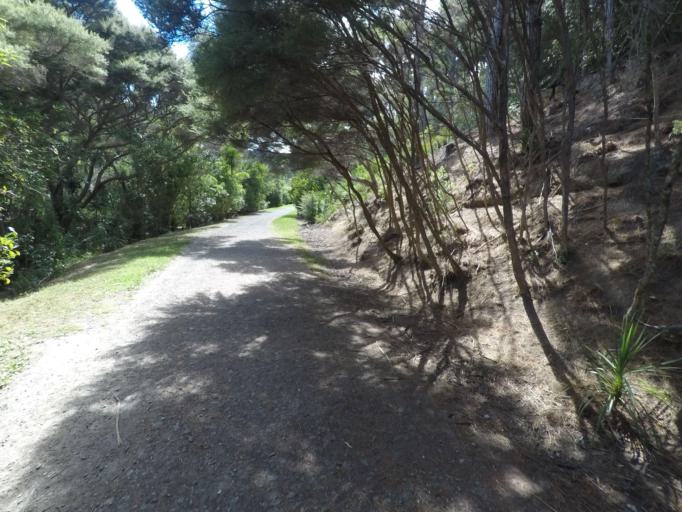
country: NZ
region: Auckland
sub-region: Auckland
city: North Shore
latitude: -36.8138
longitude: 174.6982
